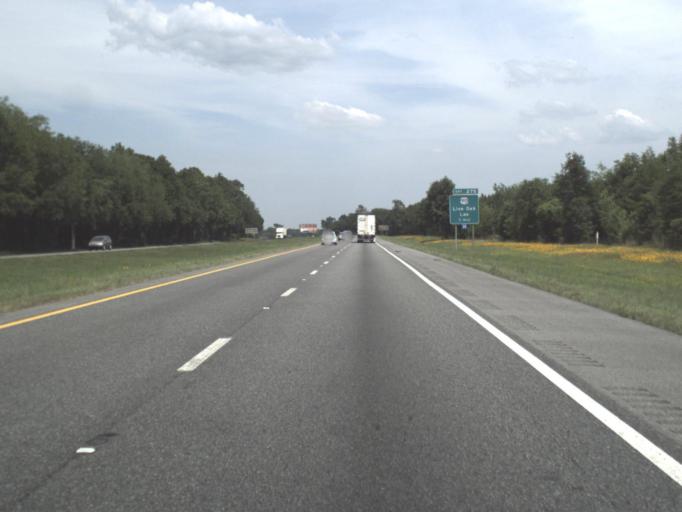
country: US
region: Florida
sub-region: Suwannee County
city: Live Oak
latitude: 30.3383
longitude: -83.1124
